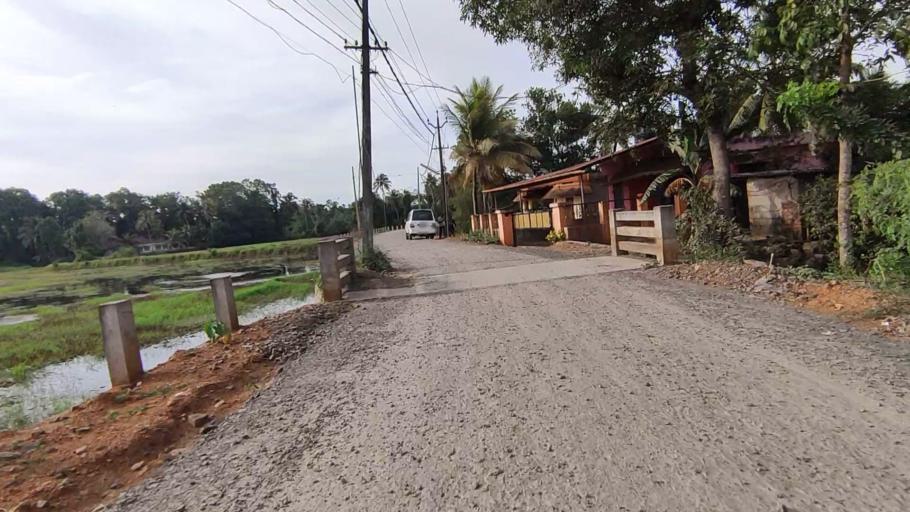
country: IN
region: Kerala
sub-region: Kottayam
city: Kottayam
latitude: 9.5751
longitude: 76.4921
